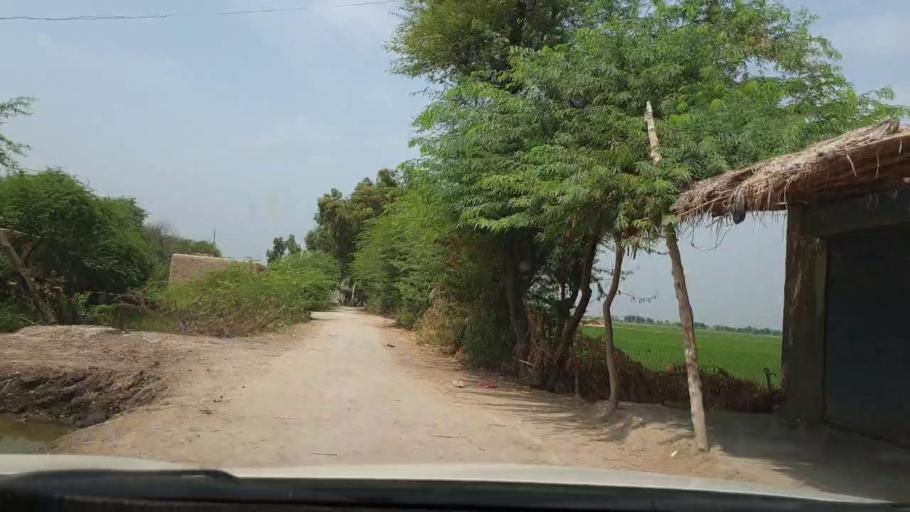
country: PK
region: Sindh
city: Goth Garelo
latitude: 27.3920
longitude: 68.0476
